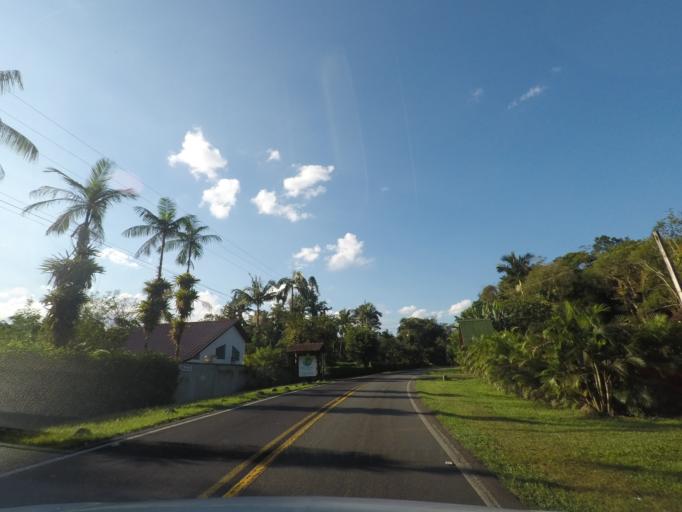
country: BR
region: Parana
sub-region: Antonina
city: Antonina
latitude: -25.3993
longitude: -48.8721
